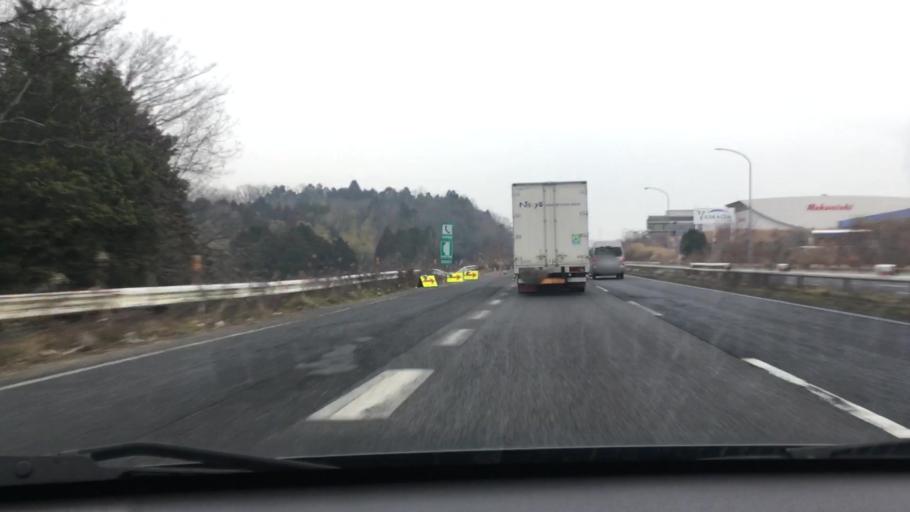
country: JP
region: Mie
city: Ueno-ebisumachi
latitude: 34.7079
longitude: 136.0768
